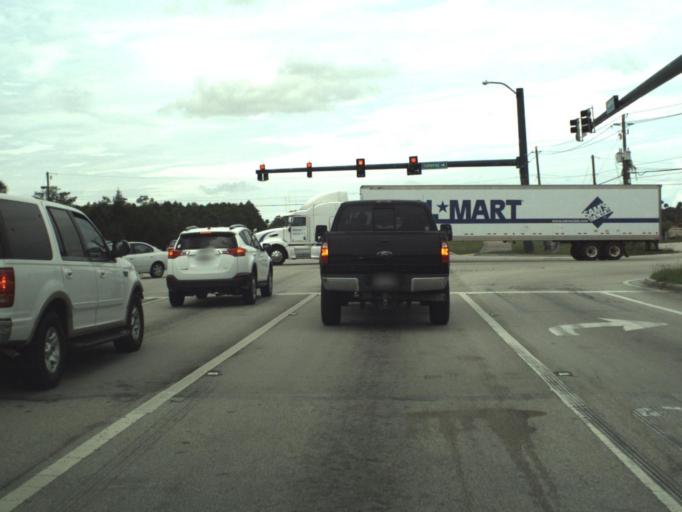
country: US
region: Florida
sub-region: Palm Beach County
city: Limestone Creek
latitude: 26.9350
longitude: -80.1575
